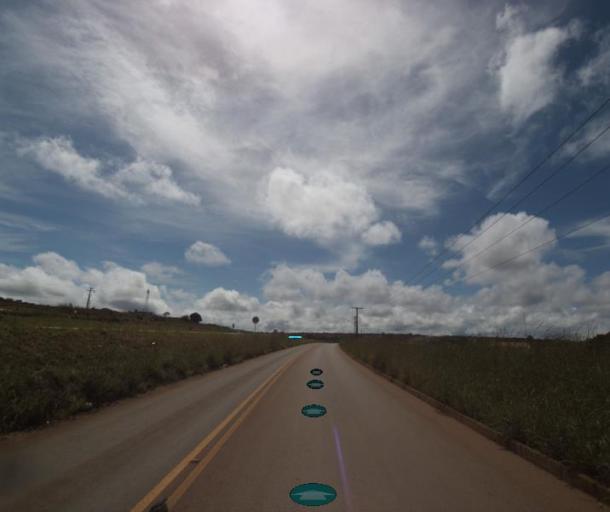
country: BR
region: Federal District
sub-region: Brasilia
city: Brasilia
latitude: -15.7422
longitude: -48.3144
